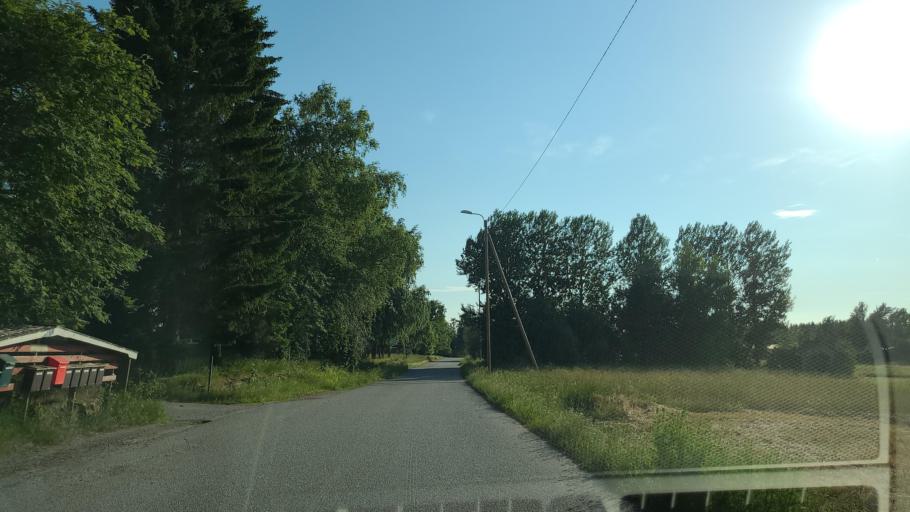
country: FI
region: Ostrobothnia
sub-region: Vaasa
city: Replot
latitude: 63.3475
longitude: 21.3316
